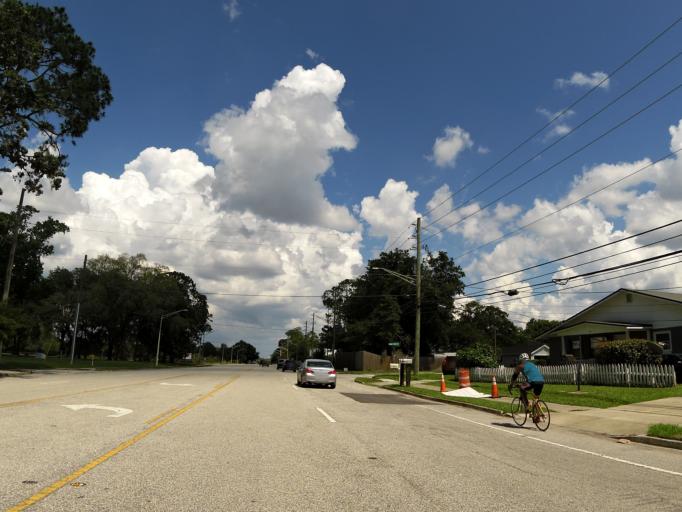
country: US
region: Florida
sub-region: Saint Johns County
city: Fruit Cove
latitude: 30.1460
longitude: -81.5652
